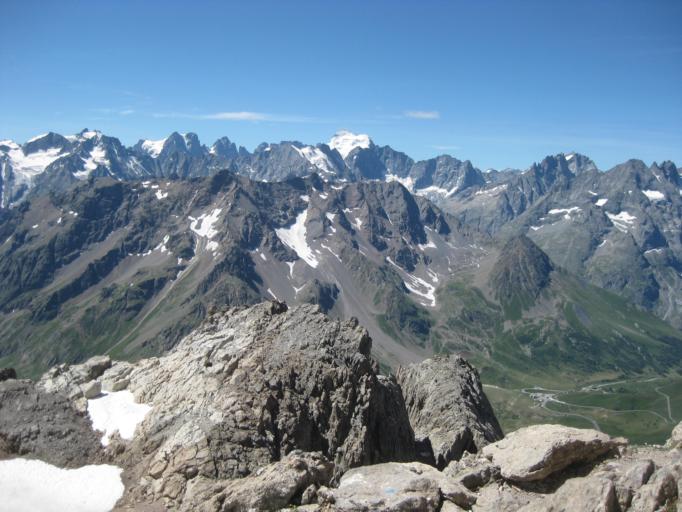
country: FR
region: Rhone-Alpes
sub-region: Departement de la Savoie
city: Valloire
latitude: 45.0635
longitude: 6.4348
